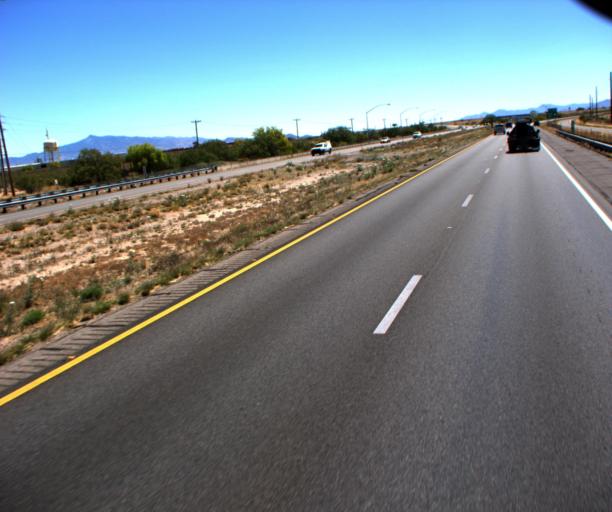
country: US
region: Arizona
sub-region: Pima County
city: Summit
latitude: 32.1092
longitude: -110.8497
